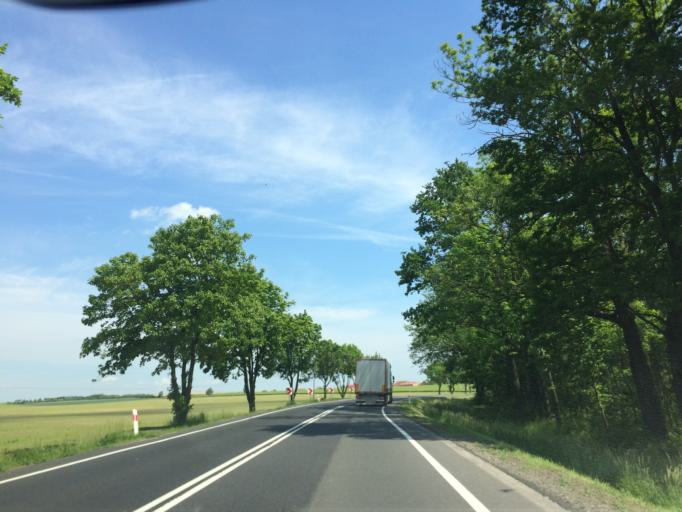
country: PL
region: Lower Silesian Voivodeship
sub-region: Powiat wroclawski
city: Gniechowice
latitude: 50.9596
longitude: 16.7871
